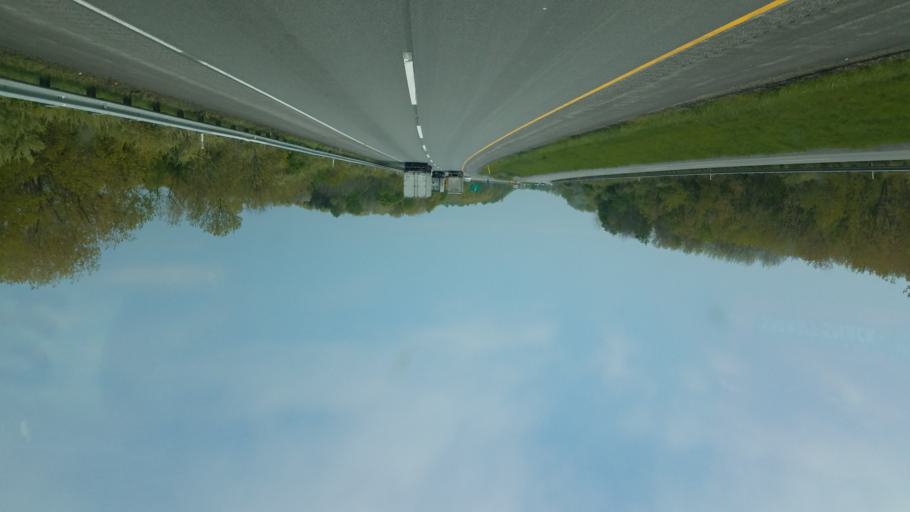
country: US
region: Indiana
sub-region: LaPorte County
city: Westville
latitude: 41.6053
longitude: -86.8595
